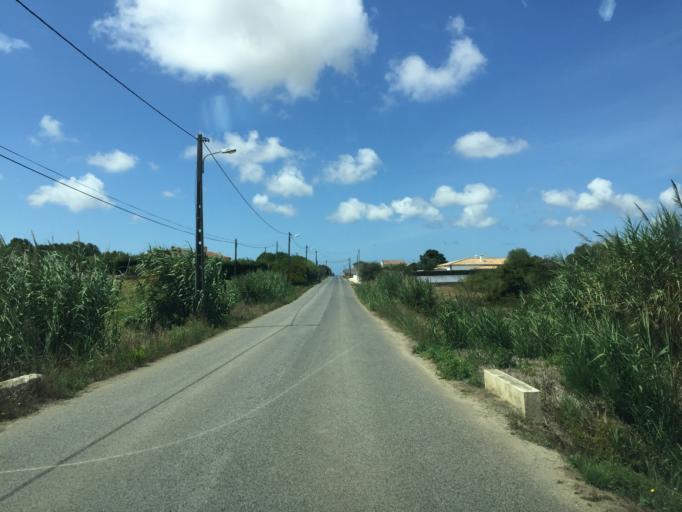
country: PT
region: Leiria
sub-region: Bombarral
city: Bombarral
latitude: 39.2797
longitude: -9.2408
